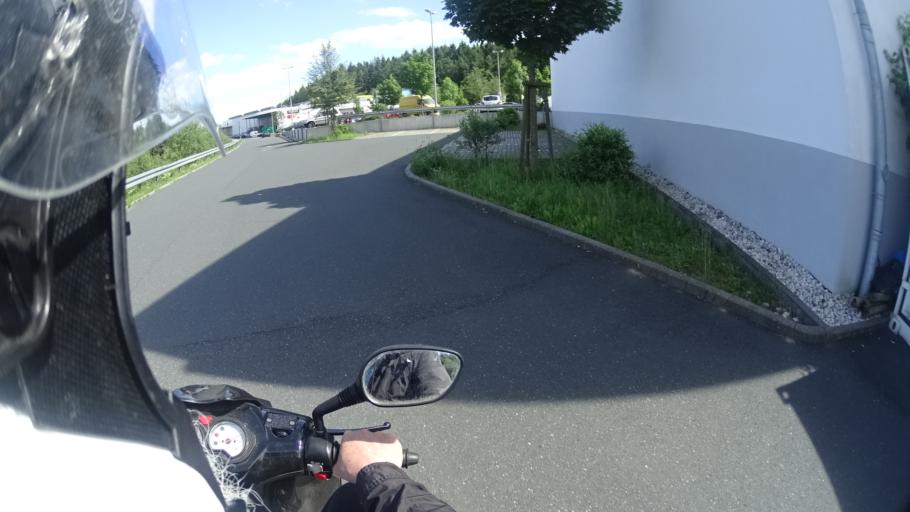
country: DE
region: Hesse
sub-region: Regierungsbezirk Darmstadt
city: Bad Schwalbach
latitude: 50.1442
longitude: 8.0434
